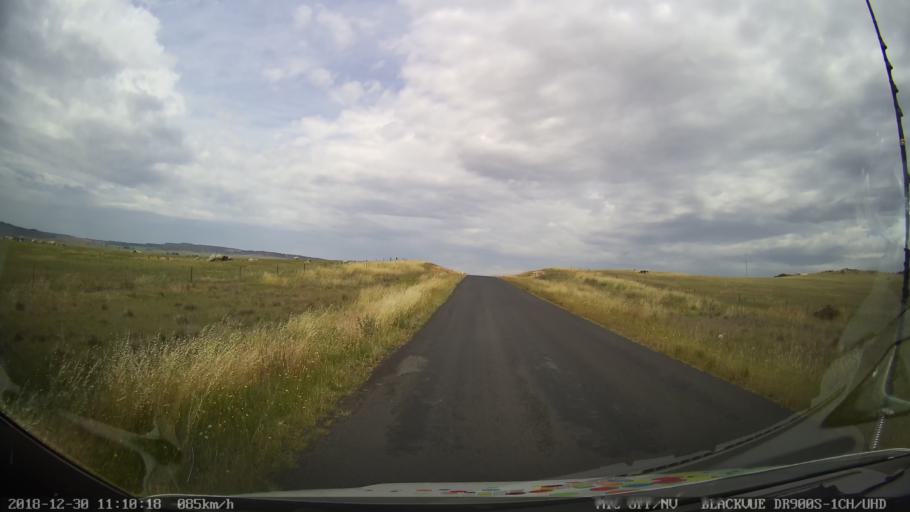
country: AU
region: New South Wales
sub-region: Snowy River
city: Berridale
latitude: -36.5136
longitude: 148.7828
